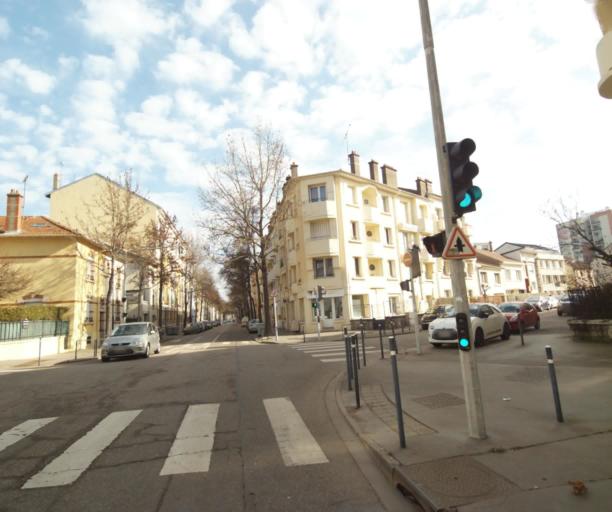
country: FR
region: Lorraine
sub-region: Departement de Meurthe-et-Moselle
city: Nancy
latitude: 48.6734
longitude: 6.1780
